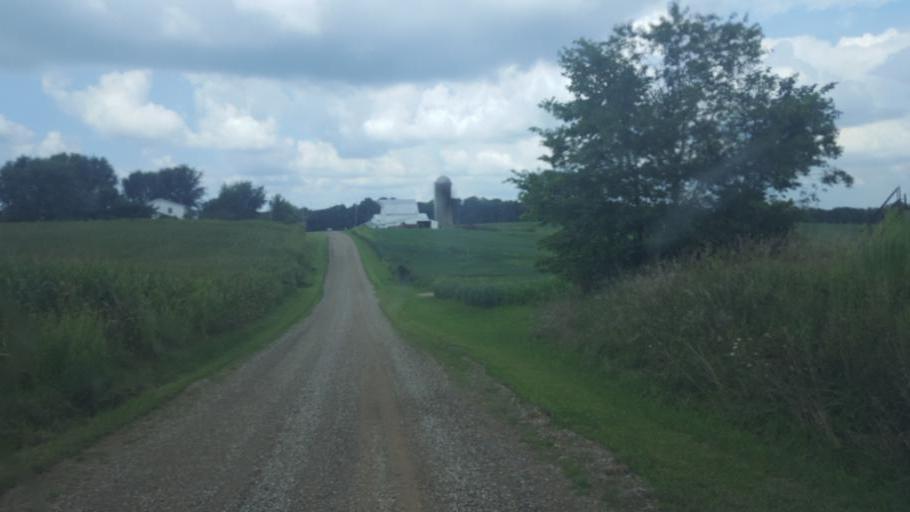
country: US
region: Ohio
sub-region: Knox County
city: Gambier
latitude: 40.3728
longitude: -82.3237
